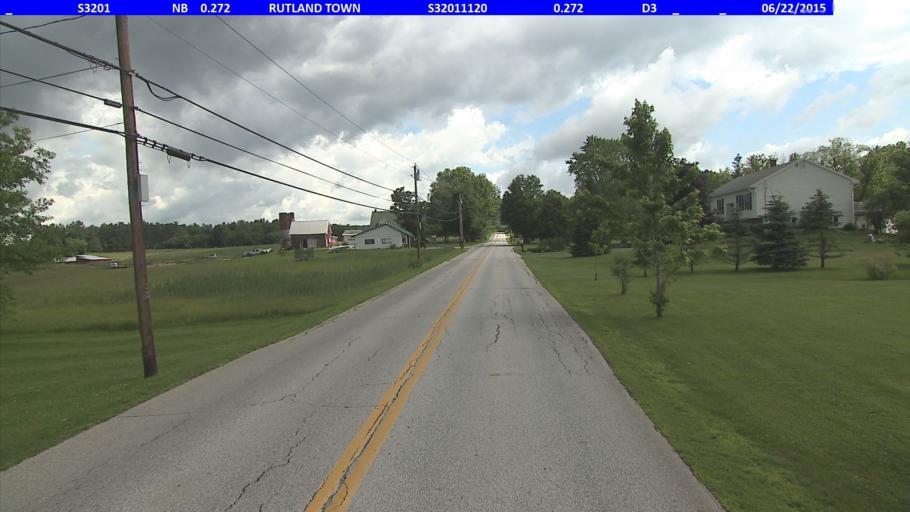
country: US
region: Vermont
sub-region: Rutland County
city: Rutland
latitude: 43.6418
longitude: -72.9748
